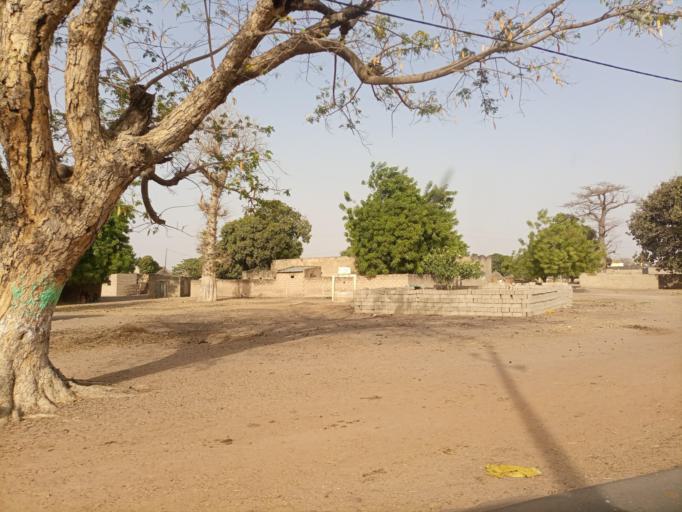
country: SN
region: Fatick
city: Passi
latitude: 14.0362
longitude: -16.3168
